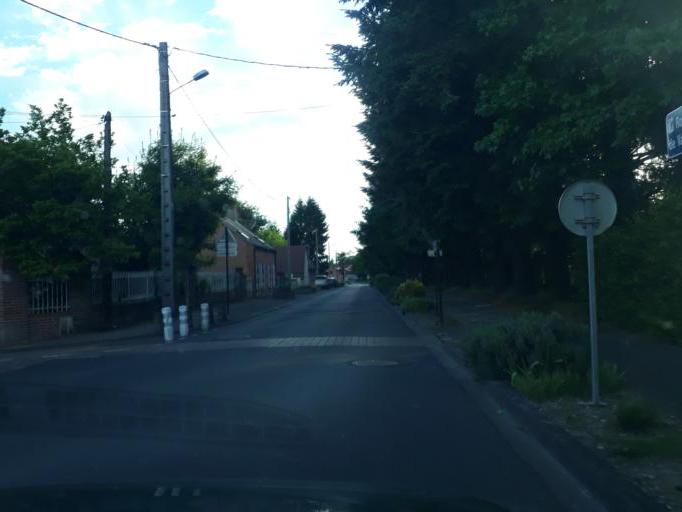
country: FR
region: Centre
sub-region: Departement du Loiret
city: La Ferte-Saint-Aubin
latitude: 47.7226
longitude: 1.9474
